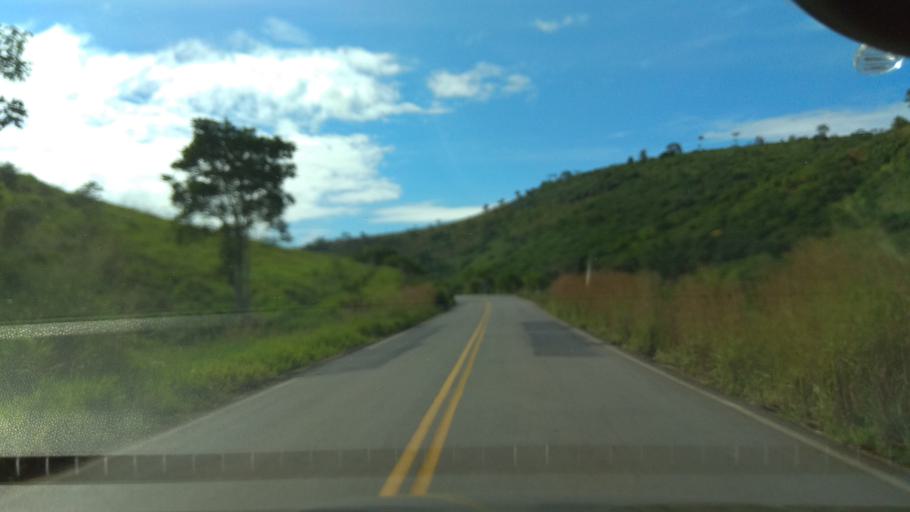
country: BR
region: Bahia
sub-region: Ubaira
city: Ubaira
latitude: -13.2631
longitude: -39.6807
